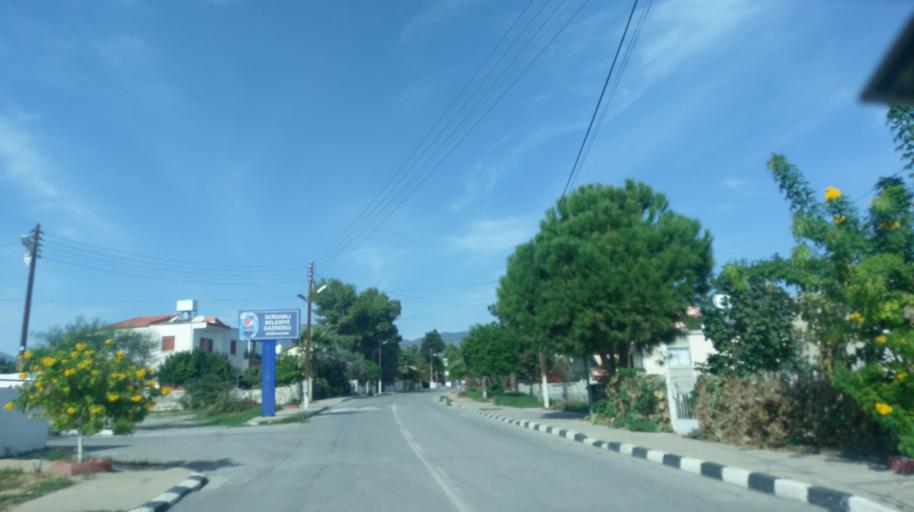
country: CY
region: Ammochostos
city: Lefkonoiko
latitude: 35.2483
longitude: 33.6066
